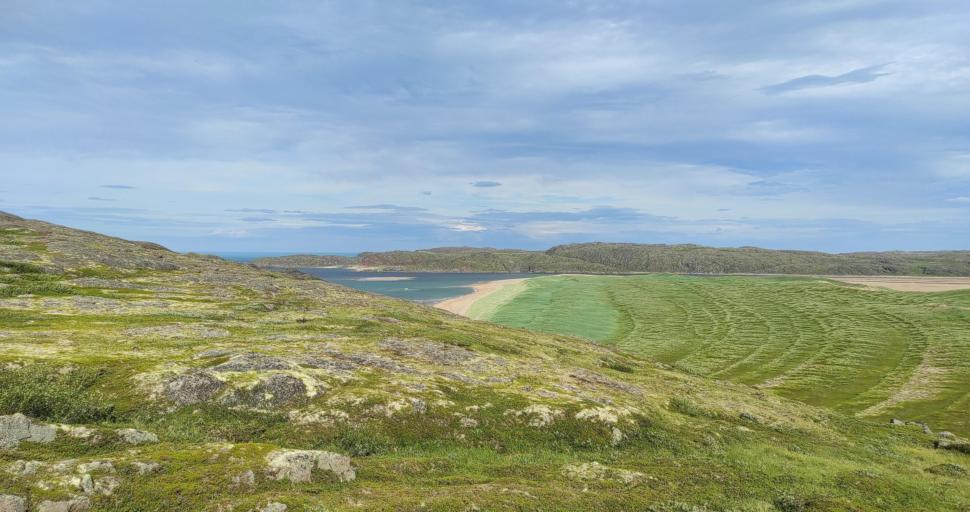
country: RU
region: Murmansk
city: Teriberka
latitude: 69.1754
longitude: 35.7575
